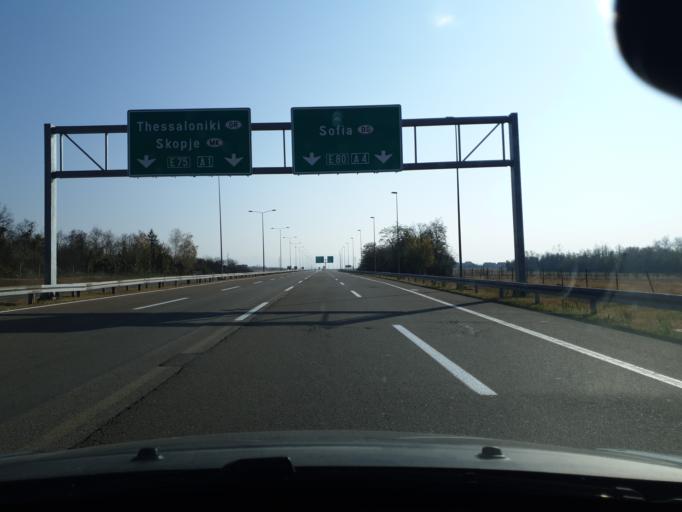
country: RS
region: Central Serbia
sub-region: Nisavski Okrug
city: Nis
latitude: 43.3682
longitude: 21.8186
